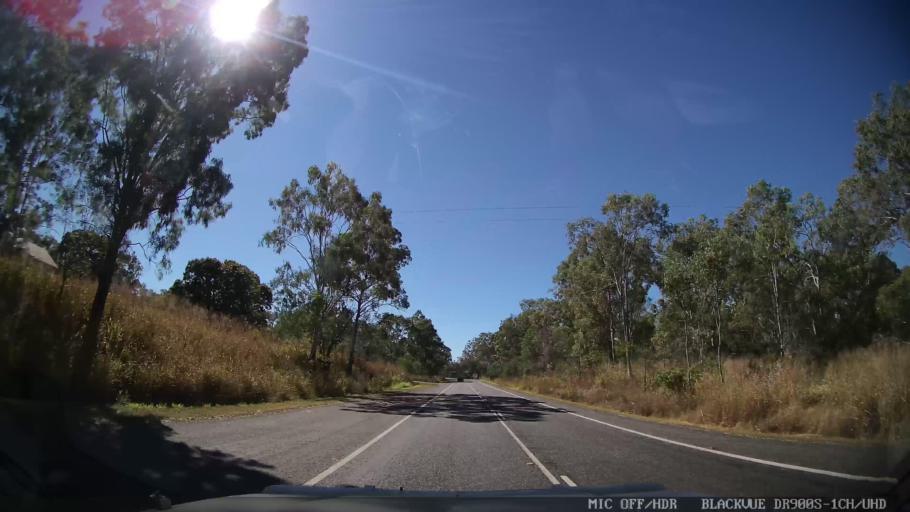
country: AU
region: Queensland
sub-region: Gladstone
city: Toolooa
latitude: -23.9579
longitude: 151.2194
